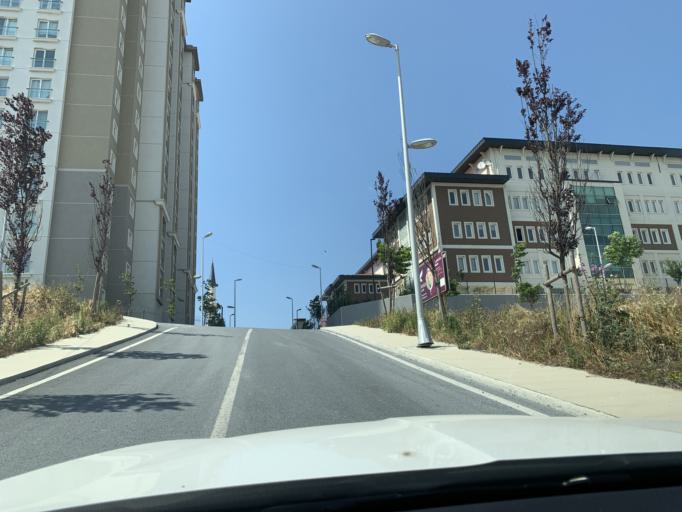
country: TR
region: Istanbul
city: Esenyurt
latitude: 41.0813
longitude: 28.6931
